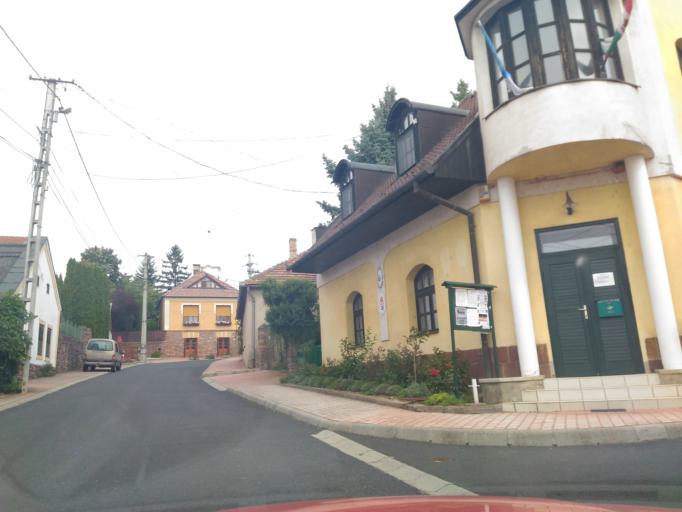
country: HU
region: Veszprem
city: Zanka
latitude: 46.8525
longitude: 17.6632
